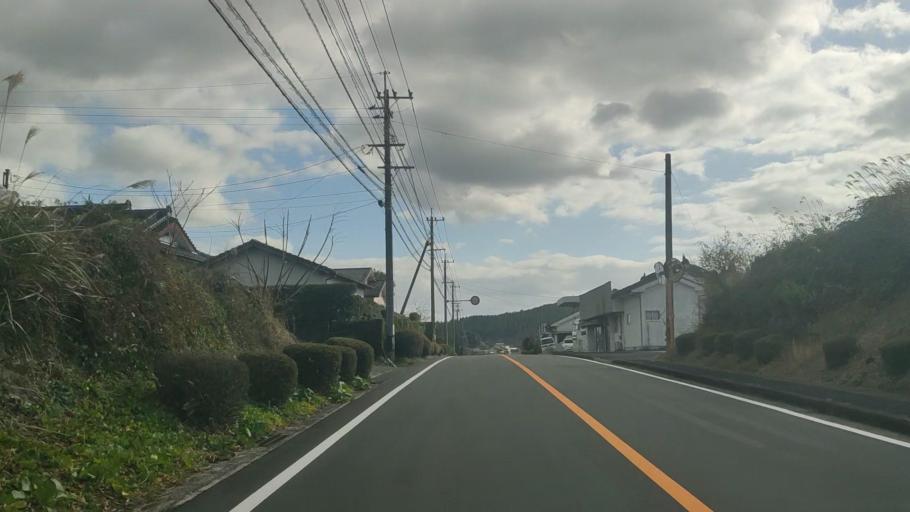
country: JP
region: Kagoshima
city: Kajiki
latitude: 31.8381
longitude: 130.6841
